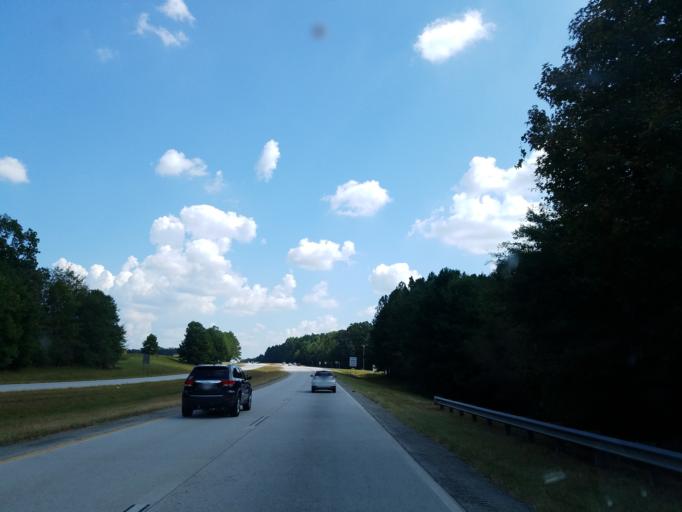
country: US
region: Georgia
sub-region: Barrow County
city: Statham
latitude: 33.9478
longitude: -83.5848
